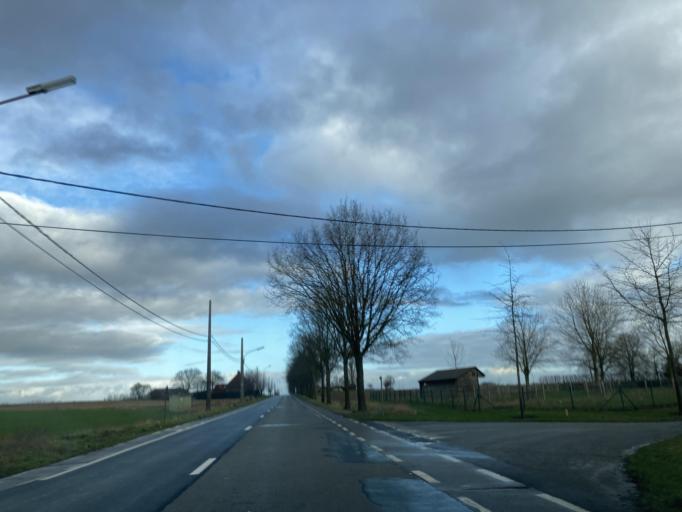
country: BE
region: Flanders
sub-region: Provincie West-Vlaanderen
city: Tielt
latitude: 51.0153
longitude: 3.3303
